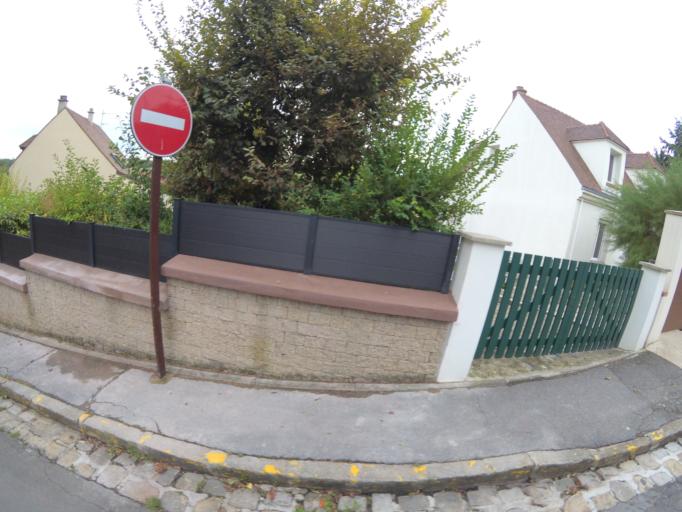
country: FR
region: Ile-de-France
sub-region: Departement de Seine-et-Marne
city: Gouvernes
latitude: 48.8625
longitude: 2.6941
